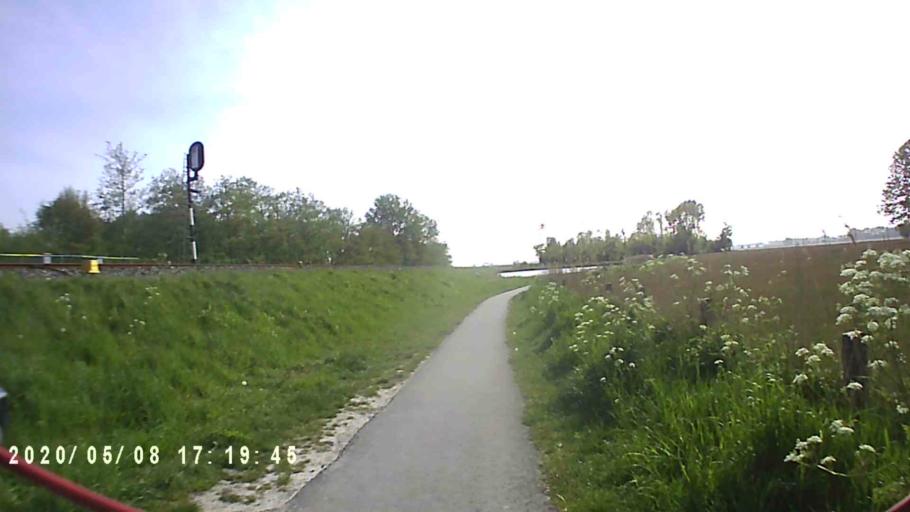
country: NL
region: Groningen
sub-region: Gemeente Winsum
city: Winsum
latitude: 53.3863
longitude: 6.5598
